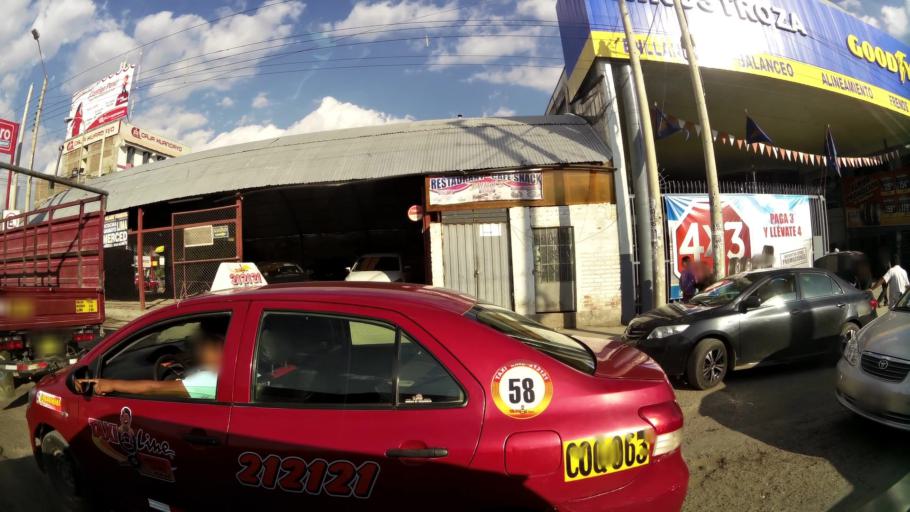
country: PE
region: Junin
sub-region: Provincia de Huancayo
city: El Tambo
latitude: -12.0544
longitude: -75.2195
